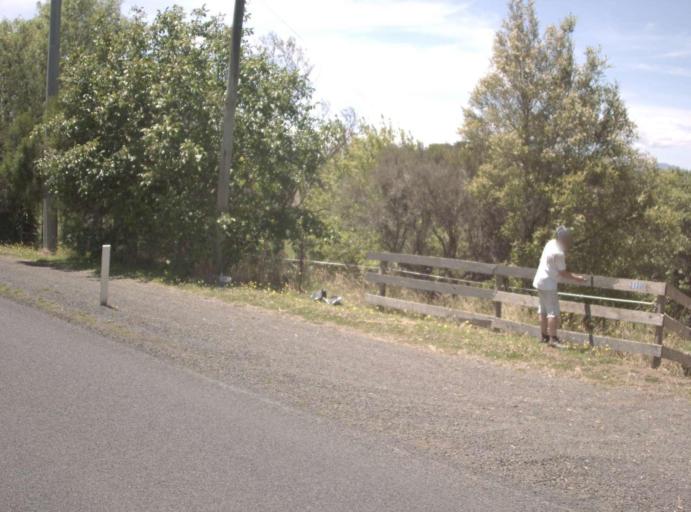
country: AU
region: Victoria
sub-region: Baw Baw
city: Warragul
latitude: -37.9993
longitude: 145.9522
